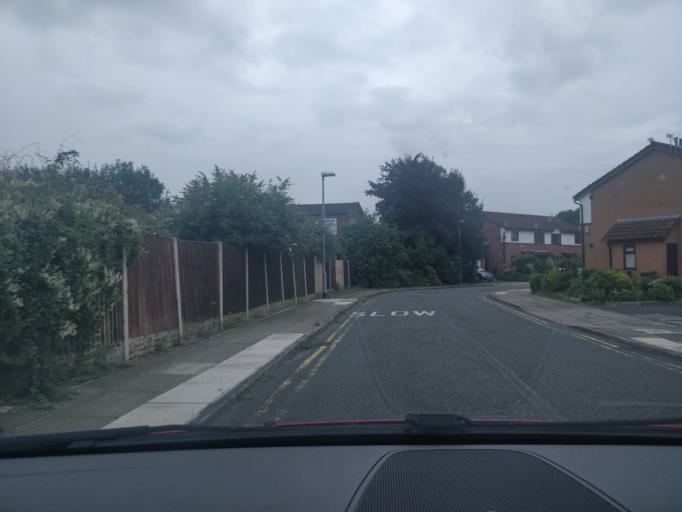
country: GB
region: England
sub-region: Sefton
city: Southport
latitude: 53.6353
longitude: -2.9812
